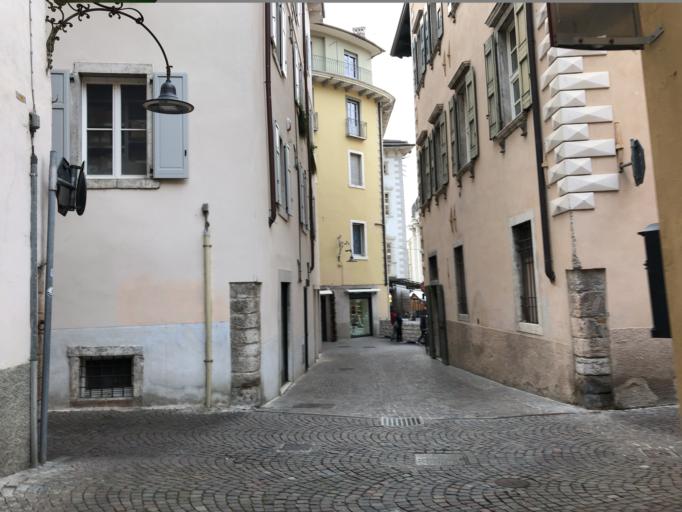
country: IT
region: Trentino-Alto Adige
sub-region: Provincia di Trento
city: Arco
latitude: 45.9197
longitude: 10.8862
